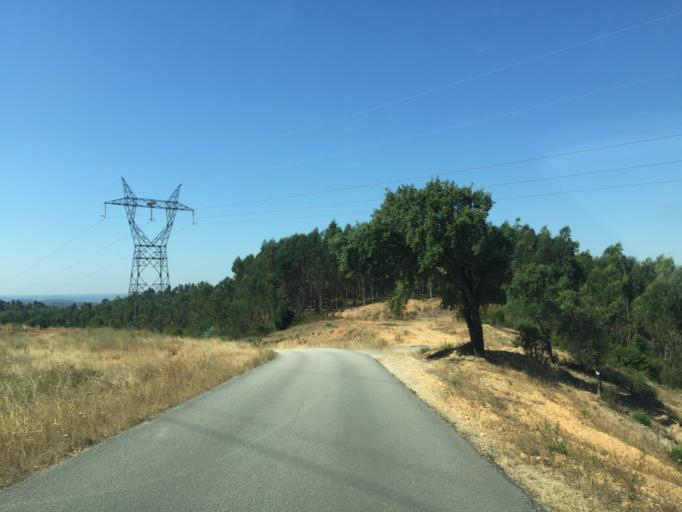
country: PT
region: Santarem
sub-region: Tomar
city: Tomar
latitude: 39.5645
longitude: -8.3208
